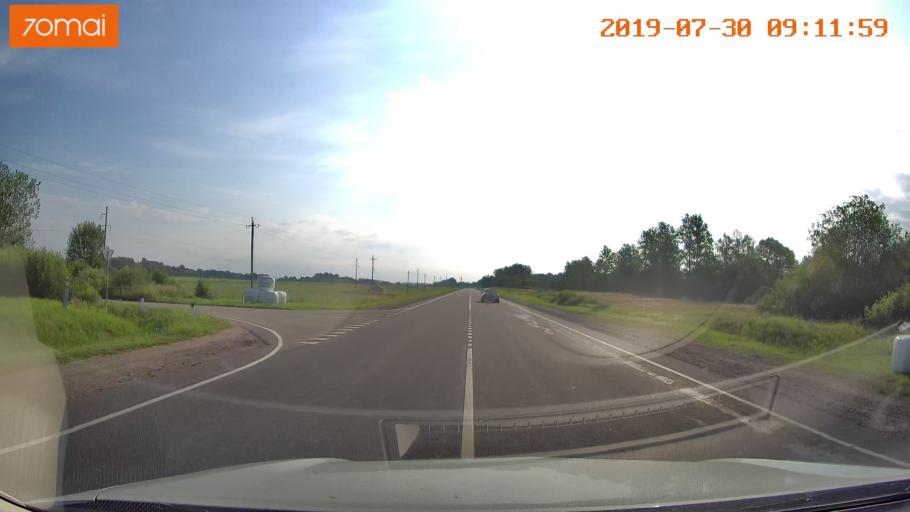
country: RU
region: Kaliningrad
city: Nesterov
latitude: 54.6151
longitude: 22.4621
